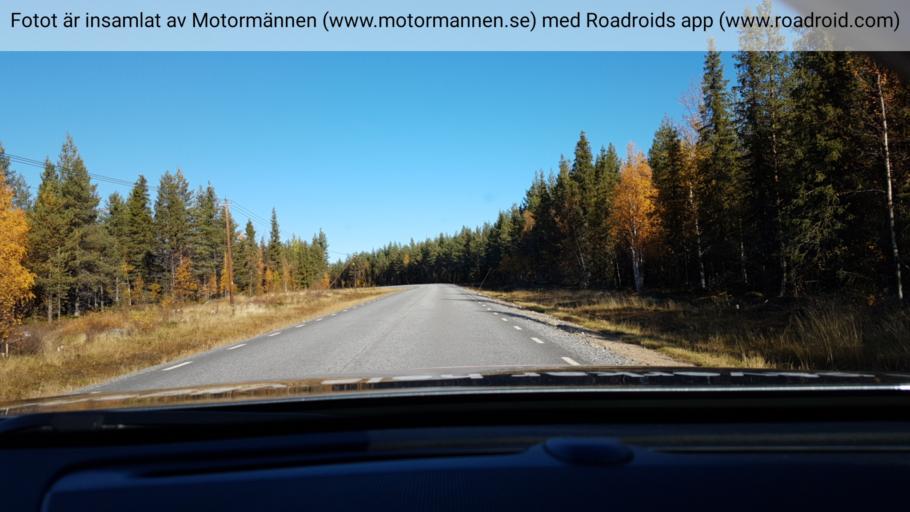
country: SE
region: Norrbotten
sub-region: Gallivare Kommun
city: Gaellivare
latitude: 66.8084
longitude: 21.0418
